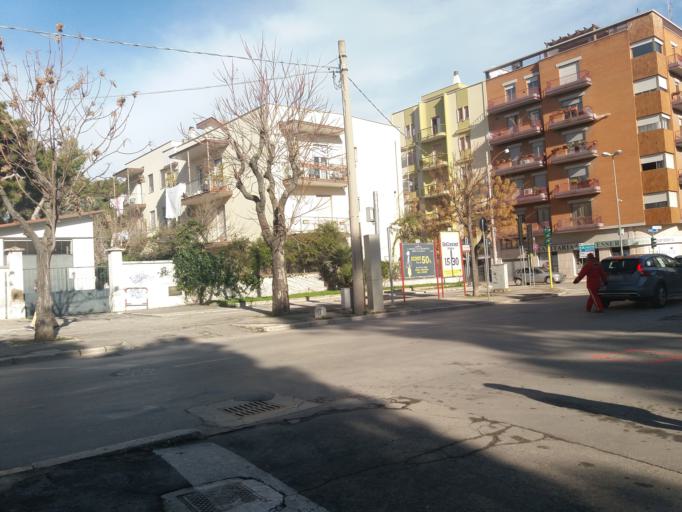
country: IT
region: Apulia
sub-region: Provincia di Barletta - Andria - Trani
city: Andria
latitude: 41.2346
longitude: 16.3087
